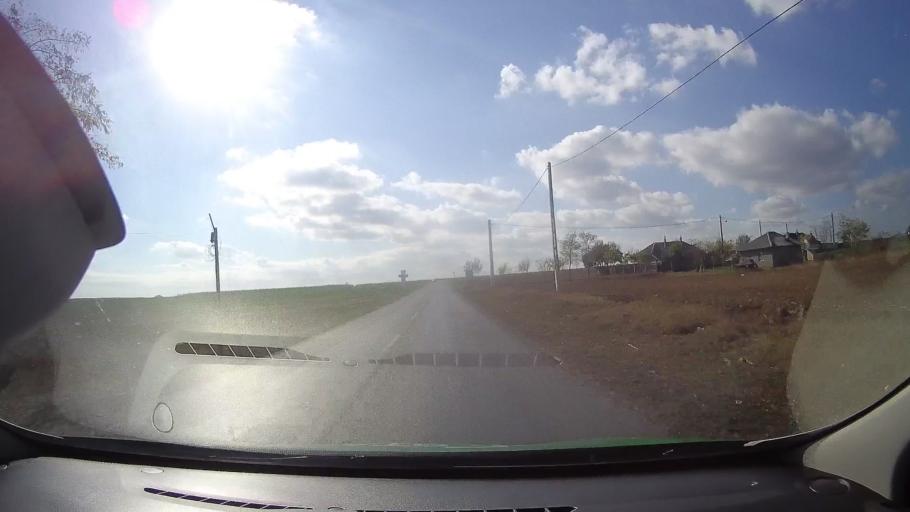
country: RO
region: Constanta
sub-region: Comuna Mihai Viteazu
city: Mihai Viteazu
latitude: 44.6224
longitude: 28.7291
